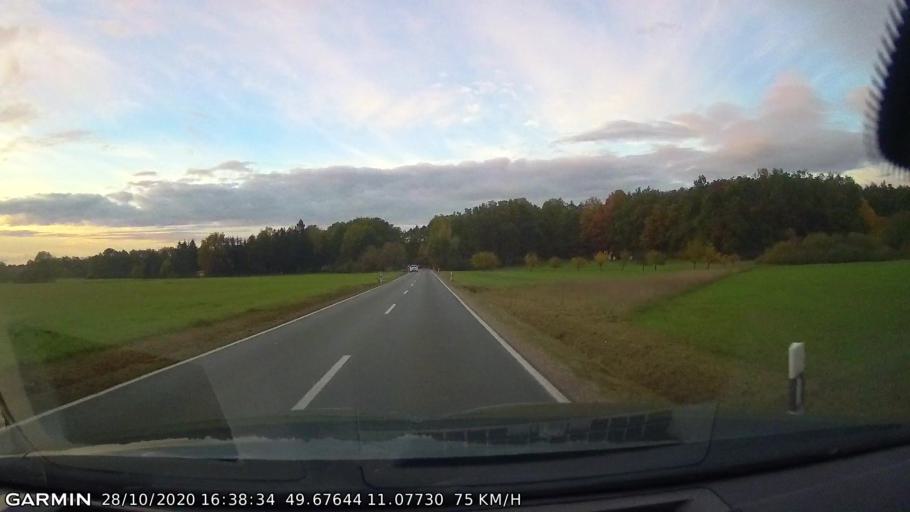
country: DE
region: Bavaria
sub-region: Upper Franconia
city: Poxdorf
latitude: 49.6766
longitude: 11.0772
